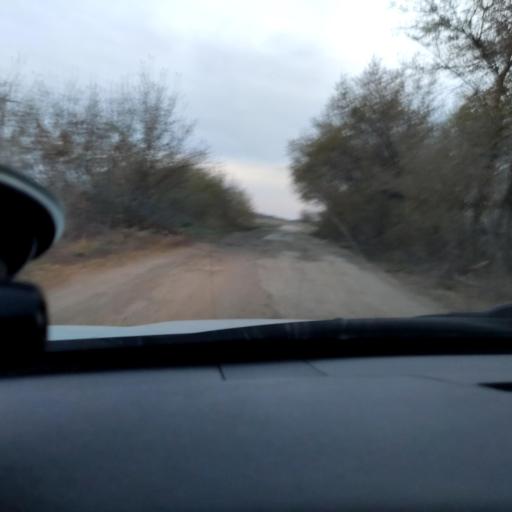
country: RU
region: Samara
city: Smyshlyayevka
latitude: 53.1518
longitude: 50.3896
